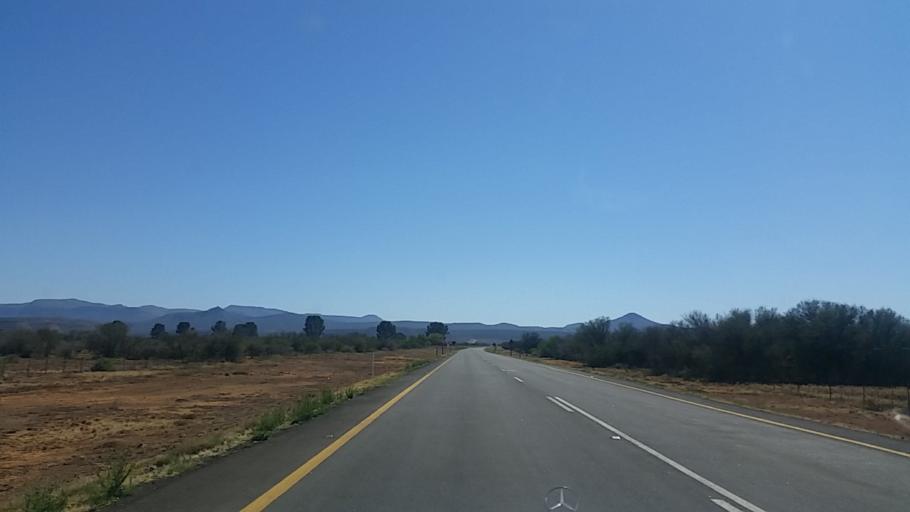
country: ZA
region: Eastern Cape
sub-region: Cacadu District Municipality
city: Graaff-Reinet
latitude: -32.1976
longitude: 24.5541
